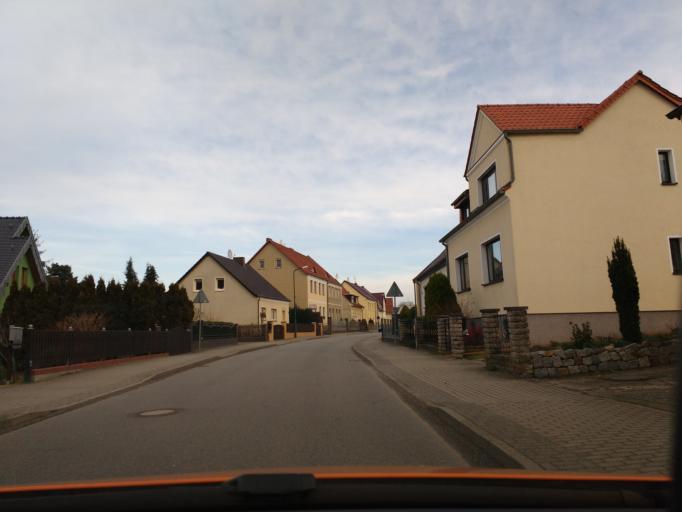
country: DE
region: Brandenburg
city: Michendorf
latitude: 52.3424
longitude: 12.9833
